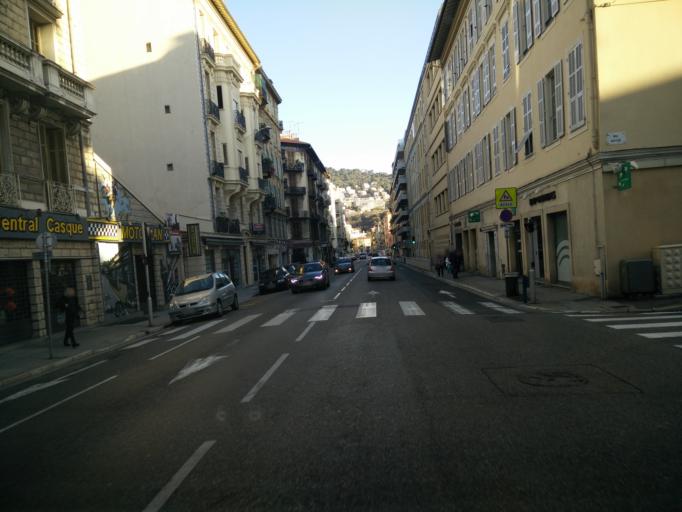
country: FR
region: Provence-Alpes-Cote d'Azur
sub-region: Departement des Alpes-Maritimes
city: Nice
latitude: 43.7021
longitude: 7.2820
